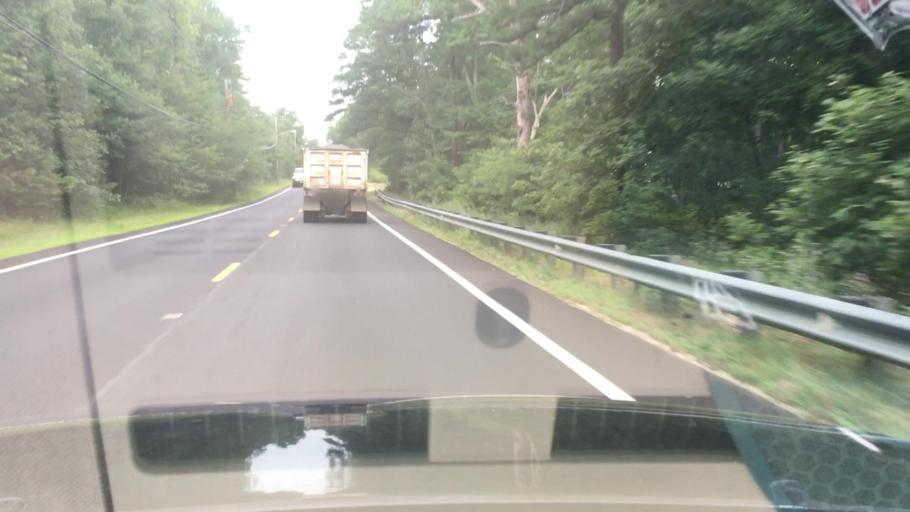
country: US
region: New Jersey
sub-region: Ocean County
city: Lakehurst
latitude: 40.0531
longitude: -74.3421
